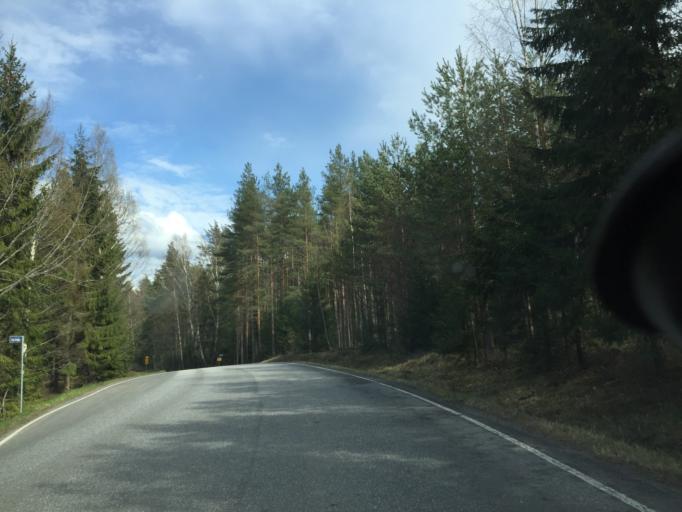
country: FI
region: Varsinais-Suomi
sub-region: Salo
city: Pernioe
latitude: 60.0412
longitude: 23.2427
